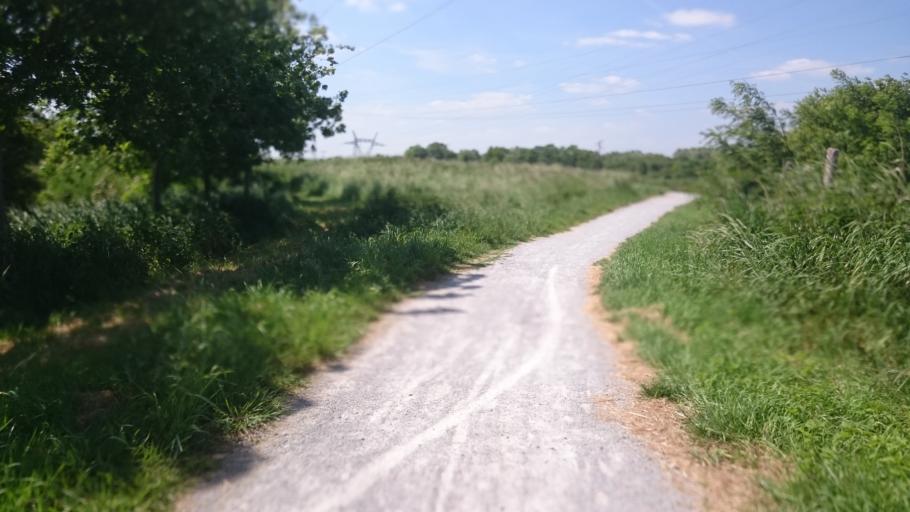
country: FR
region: Pays de la Loire
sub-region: Departement de la Loire-Atlantique
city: Bouguenais
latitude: 47.1821
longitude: -1.6243
